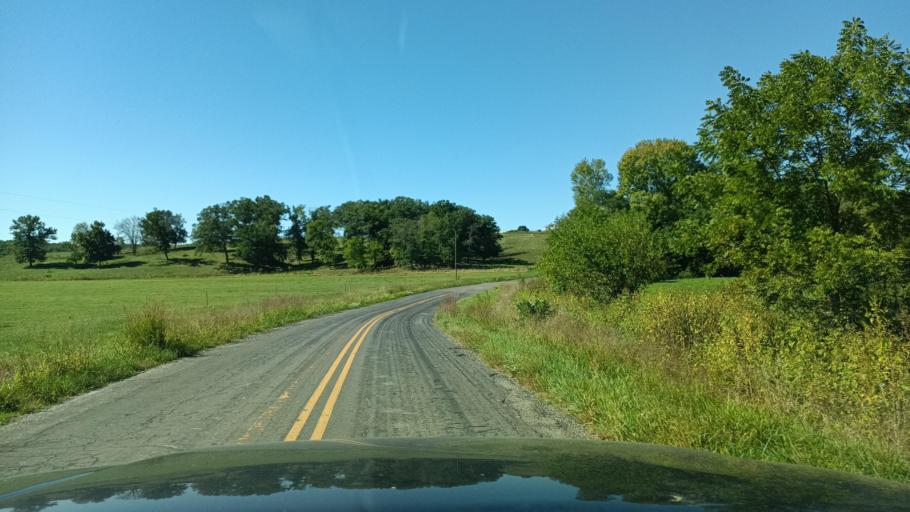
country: US
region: Missouri
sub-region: Scotland County
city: Memphis
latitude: 40.3490
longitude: -92.3241
